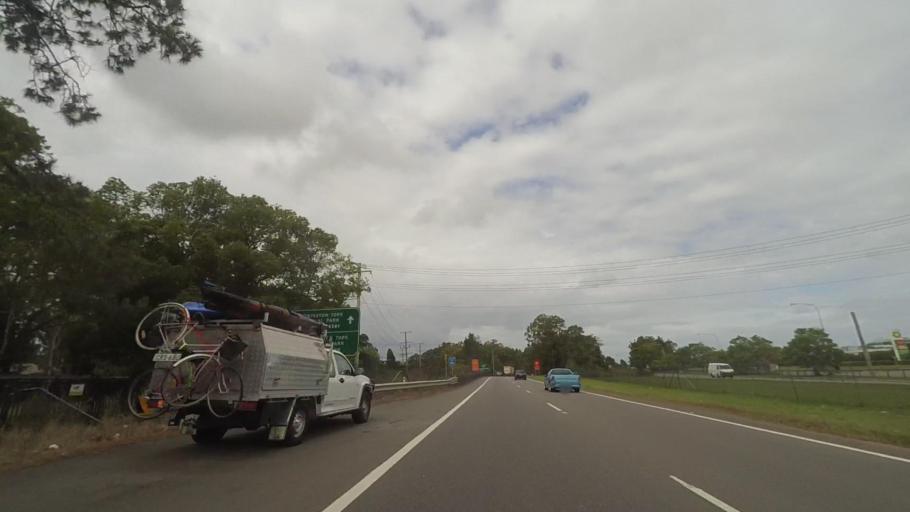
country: AU
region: New South Wales
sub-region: Port Stephens Shire
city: Raymond Terrace
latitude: -32.7829
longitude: 151.7356
